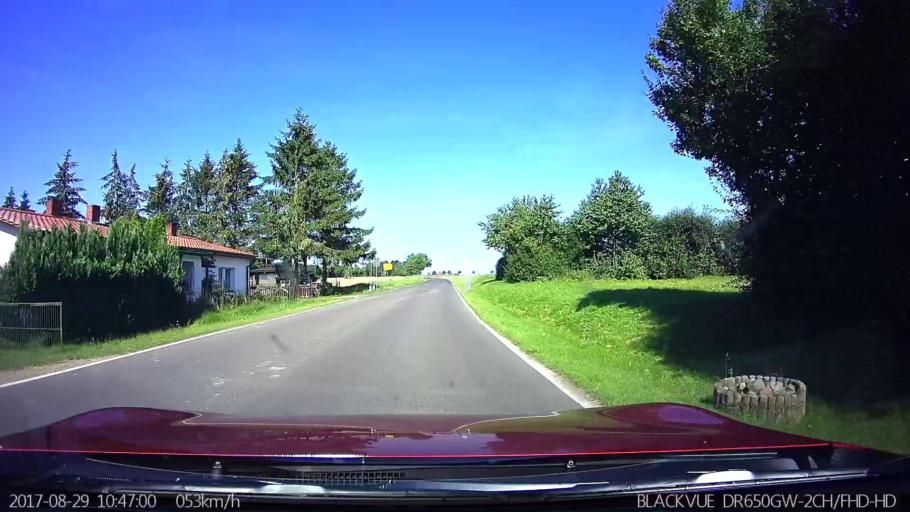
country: DE
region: Mecklenburg-Vorpommern
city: Velgast
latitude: 54.2240
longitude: 12.8339
